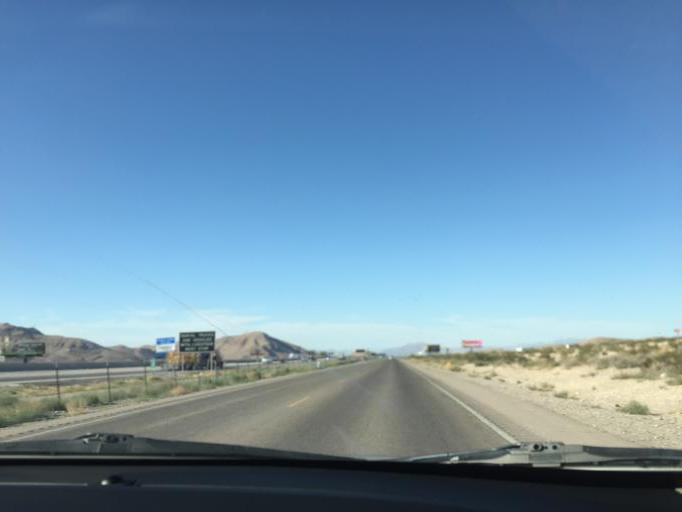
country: US
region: Nevada
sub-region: Clark County
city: Enterprise
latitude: 35.9112
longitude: -115.2061
